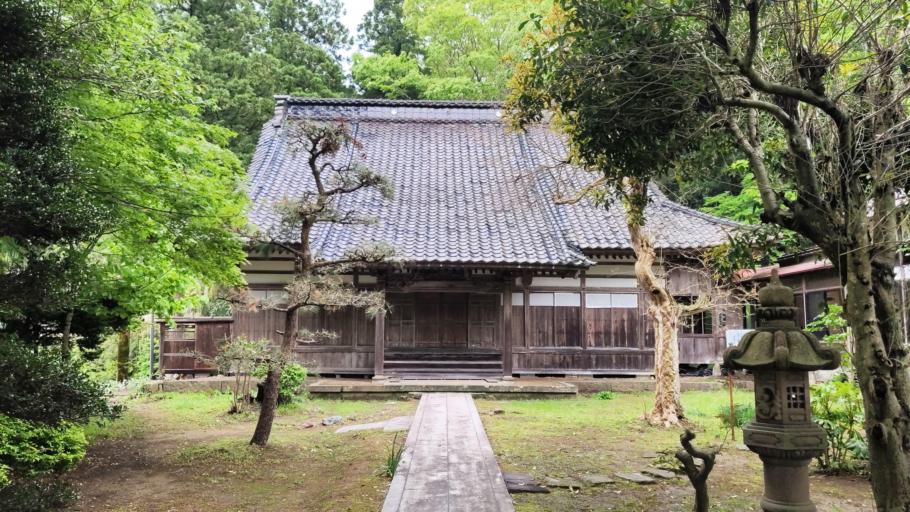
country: JP
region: Niigata
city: Kamo
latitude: 37.7120
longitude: 139.0795
